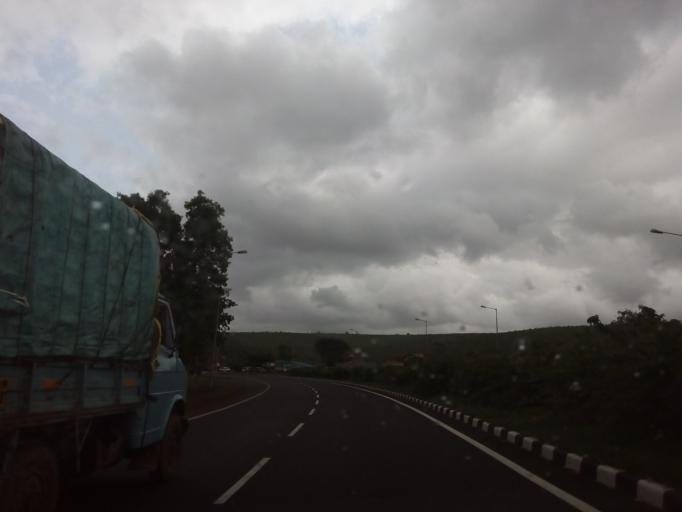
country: IN
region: Karnataka
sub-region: Belgaum
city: Hukeri
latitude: 16.0530
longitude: 74.5133
